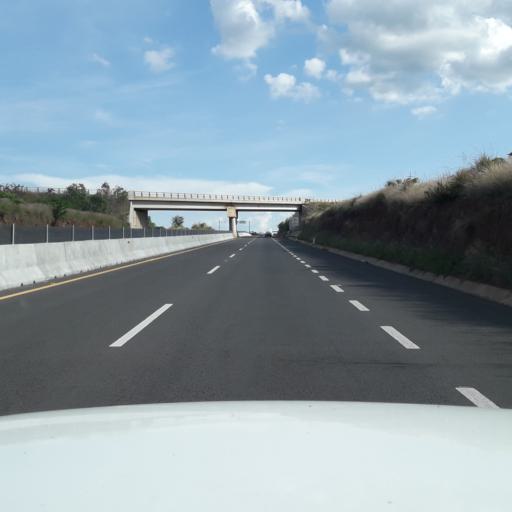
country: MX
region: Jalisco
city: Arenal
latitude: 20.7886
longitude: -103.7129
